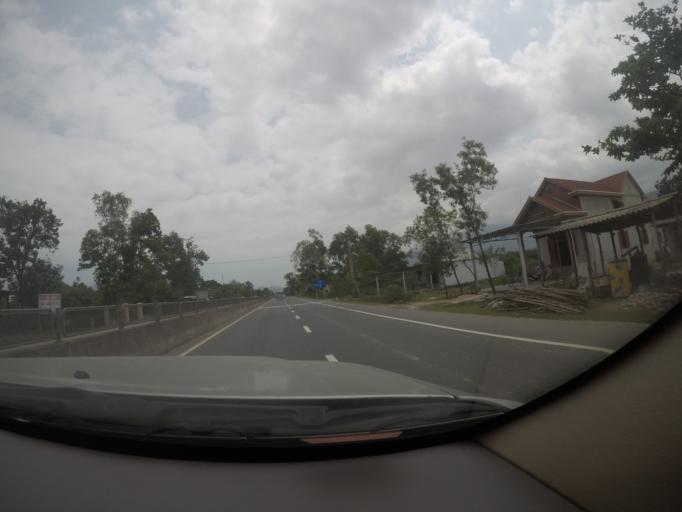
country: VN
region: Thua Thien-Hue
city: Phu Loc
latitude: 16.2722
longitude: 107.9574
